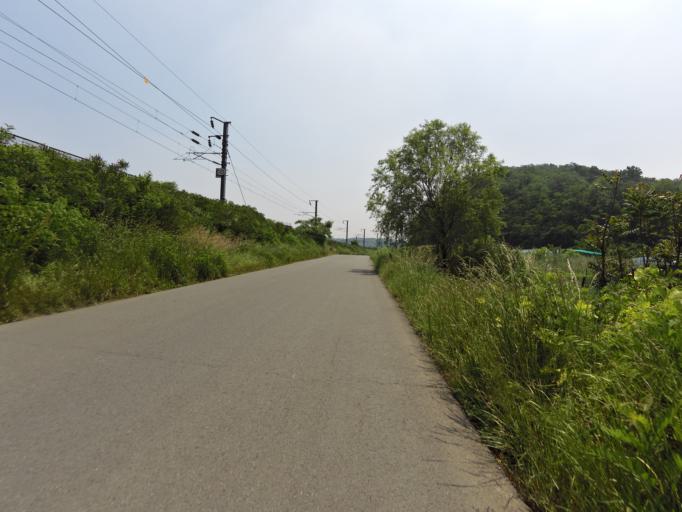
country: KR
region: Gyeongsangbuk-do
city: Gyeongsan-si
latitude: 35.8516
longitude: 128.7041
